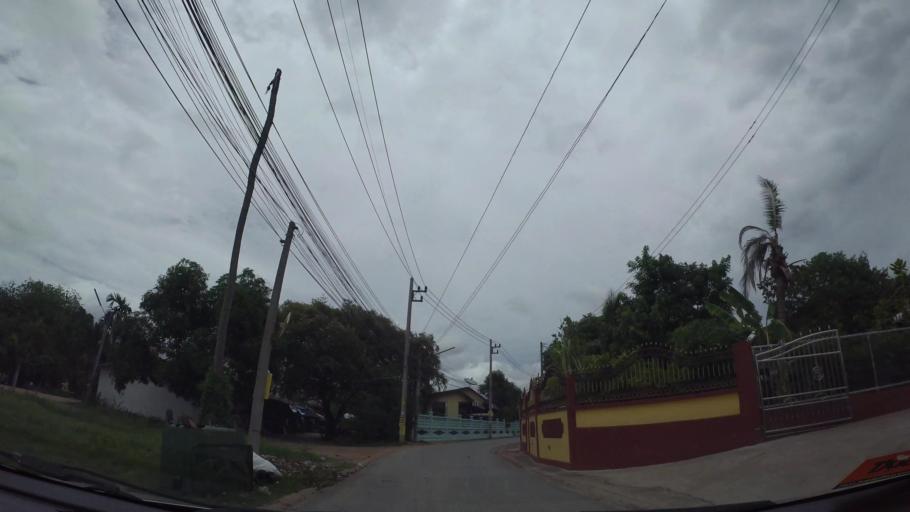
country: TH
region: Chon Buri
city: Sattahip
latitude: 12.7582
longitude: 100.8840
